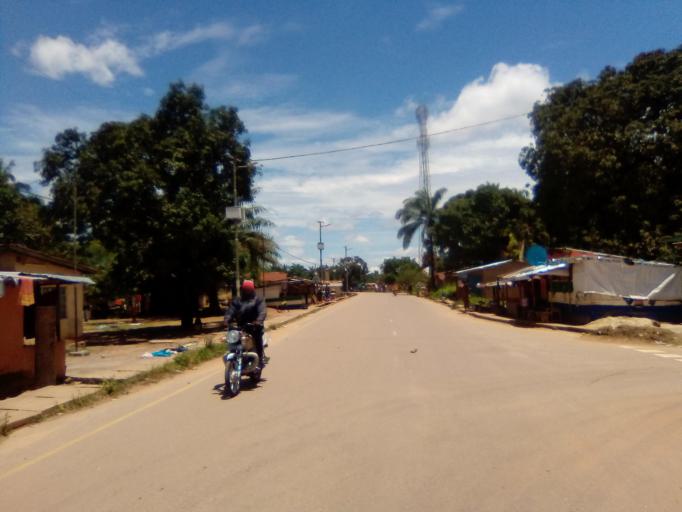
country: SL
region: Eastern Province
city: Koidu
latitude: 8.6385
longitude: -10.9695
